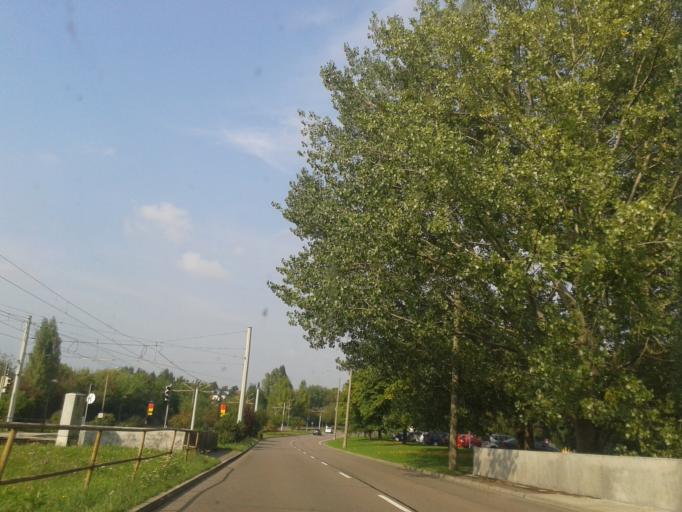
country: DE
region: Saxony
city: Freital
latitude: 51.0455
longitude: 13.6799
